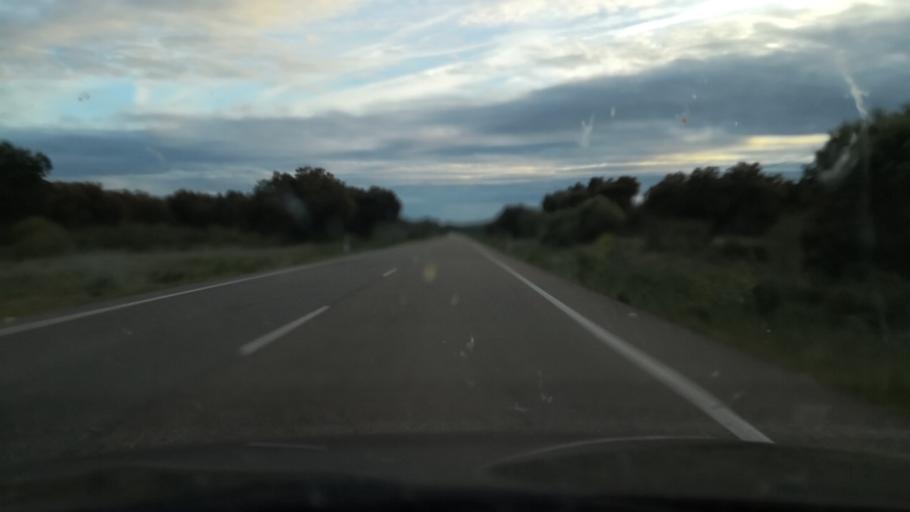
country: ES
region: Extremadura
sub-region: Provincia de Badajoz
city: La Roca de la Sierra
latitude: 39.1219
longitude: -6.6729
